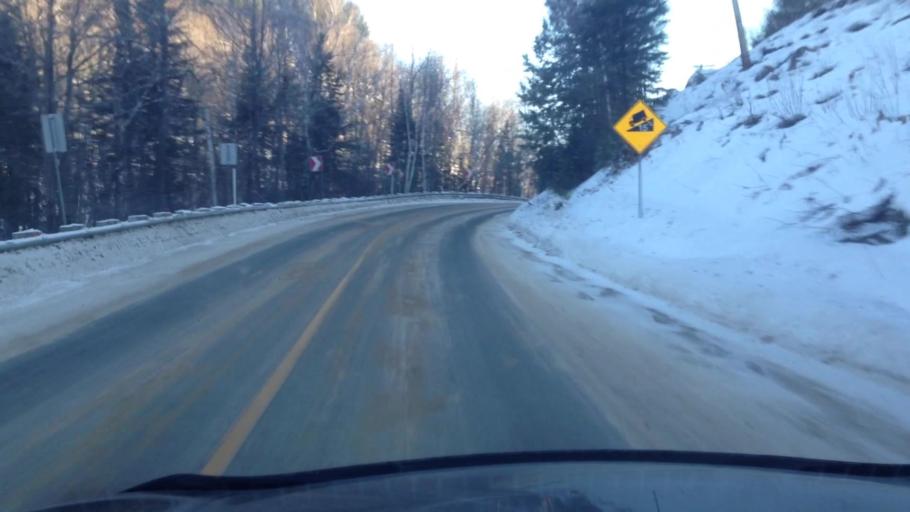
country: CA
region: Quebec
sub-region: Laurentides
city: Sainte-Agathe-des-Monts
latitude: 45.9223
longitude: -74.4852
